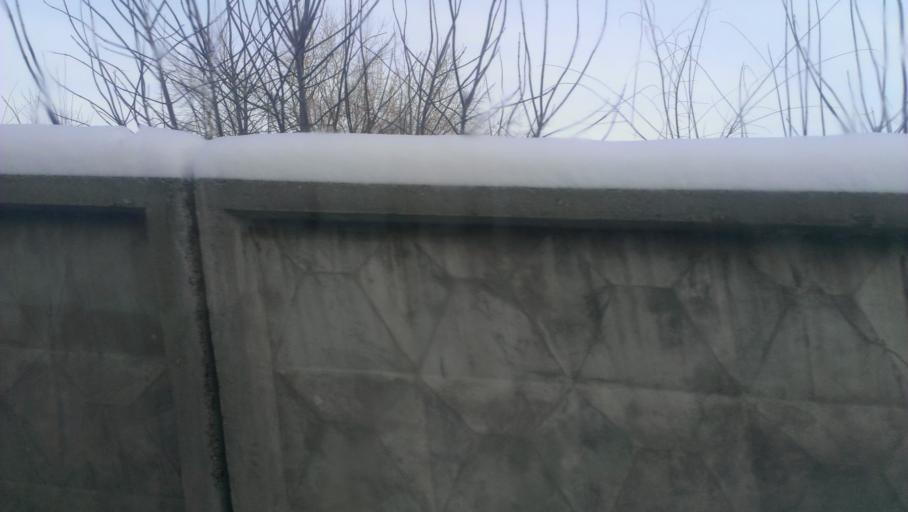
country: RU
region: Altai Krai
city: Nauchnyy Gorodok
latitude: 53.4221
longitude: 83.5198
